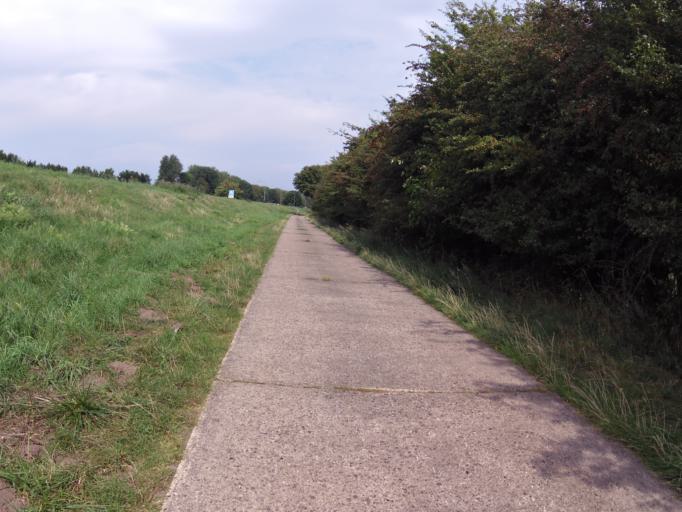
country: DE
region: Lower Saxony
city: Landesbergen
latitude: 52.5688
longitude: 9.1113
